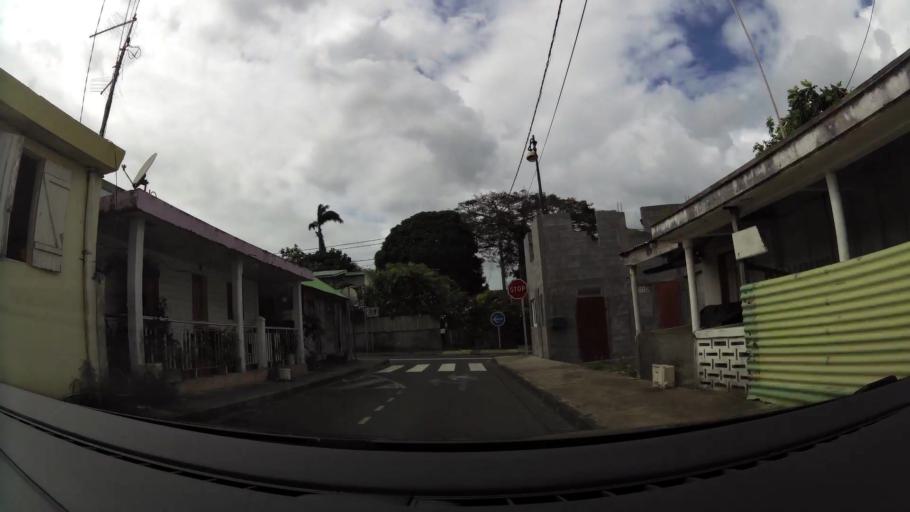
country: GP
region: Guadeloupe
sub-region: Guadeloupe
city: Baie-Mahault
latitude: 16.2666
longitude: -61.5884
